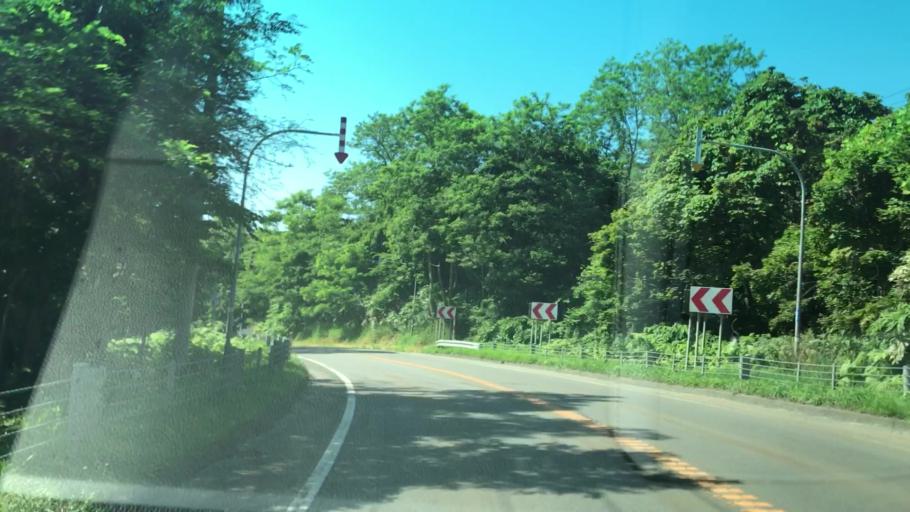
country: JP
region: Hokkaido
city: Iwanai
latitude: 43.0766
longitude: 140.4868
